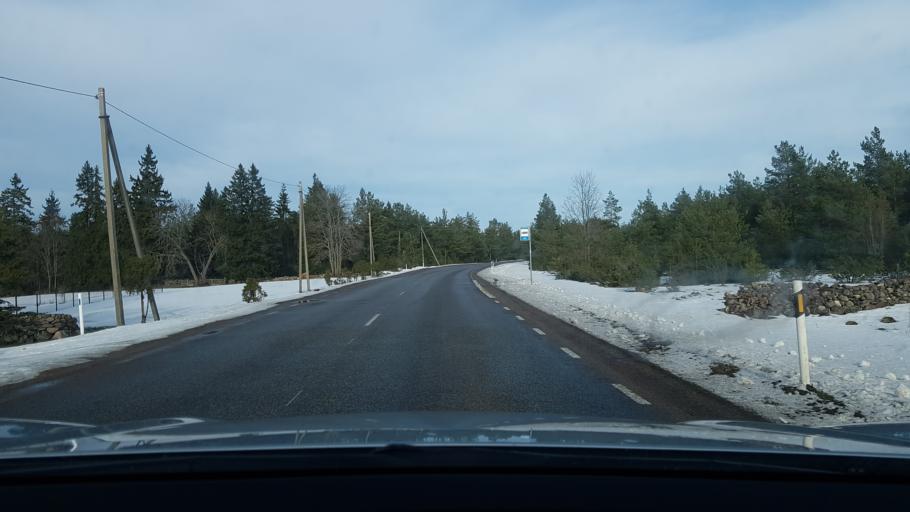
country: EE
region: Saare
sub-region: Kuressaare linn
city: Kuressaare
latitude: 58.3180
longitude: 22.5462
